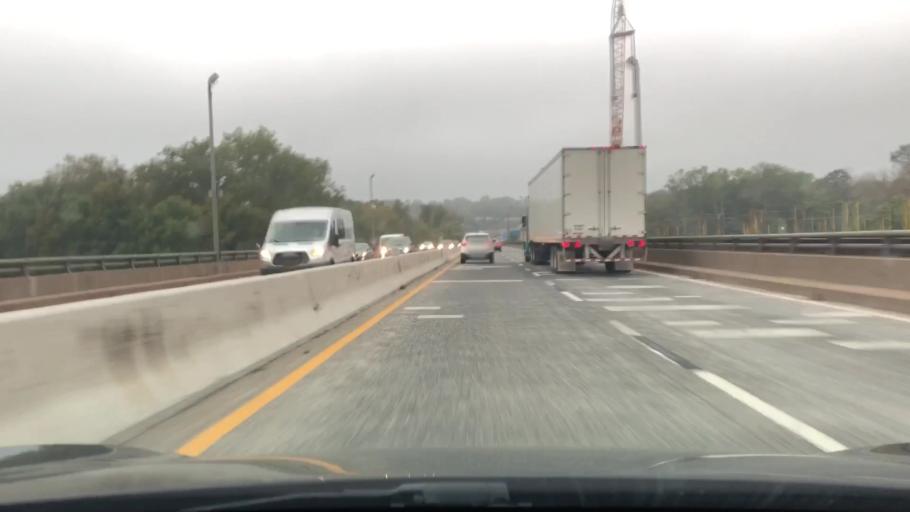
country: US
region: Pennsylvania
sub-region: Bucks County
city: Yardley
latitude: 40.2583
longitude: -74.8480
